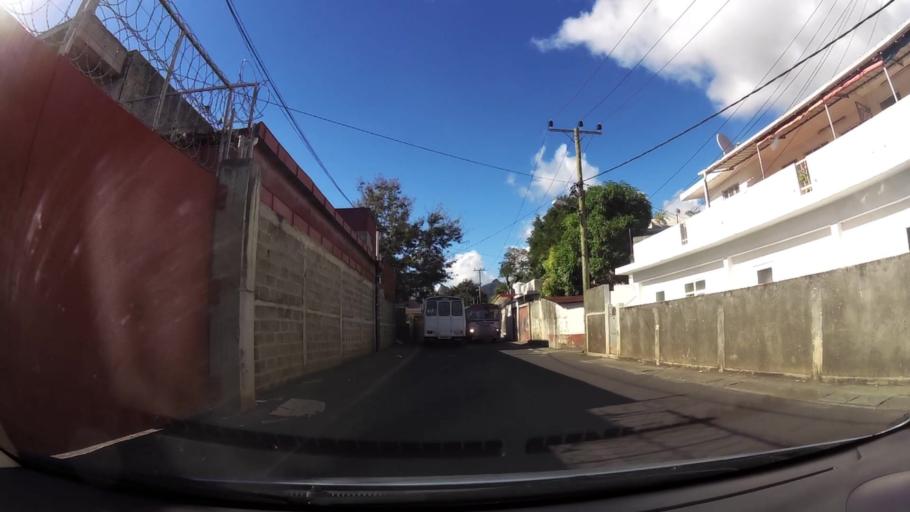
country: MU
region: Pamplemousses
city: Le Hochet
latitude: -20.1474
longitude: 57.5187
